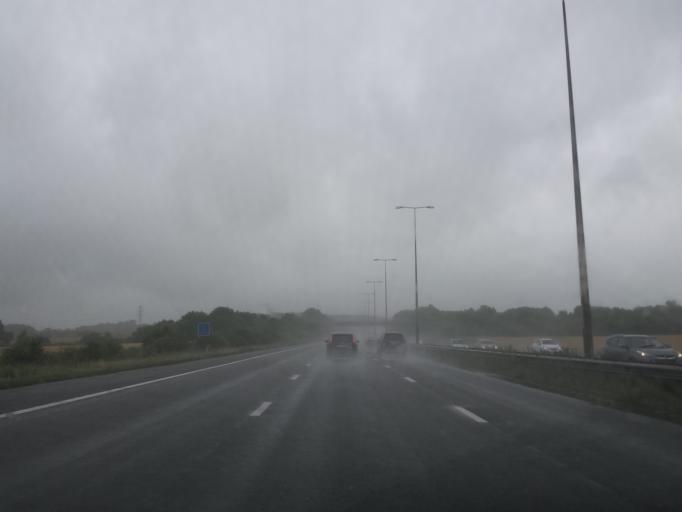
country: GB
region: England
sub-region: Leicestershire
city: Shepshed
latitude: 52.7789
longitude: -1.2802
